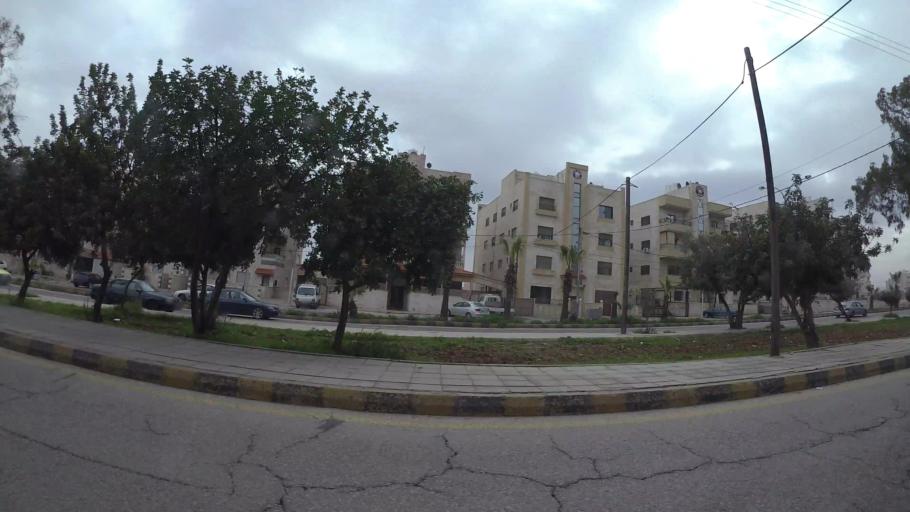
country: JO
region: Amman
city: Amman
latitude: 31.9770
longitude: 35.9334
